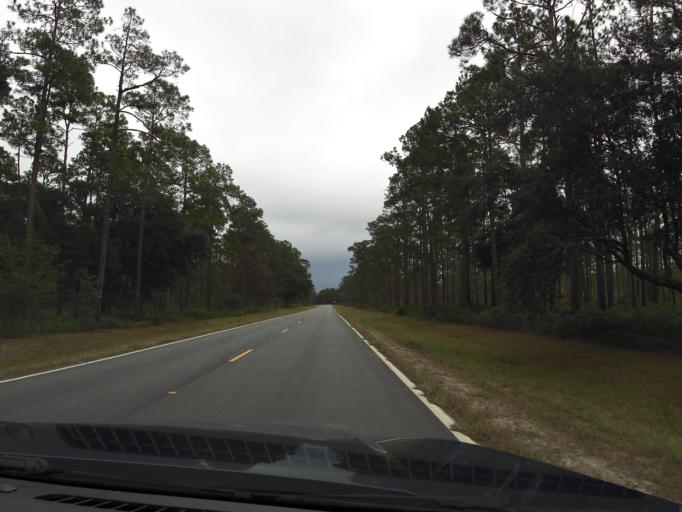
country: US
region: Georgia
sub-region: Charlton County
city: Folkston
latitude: 30.7407
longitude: -82.1232
